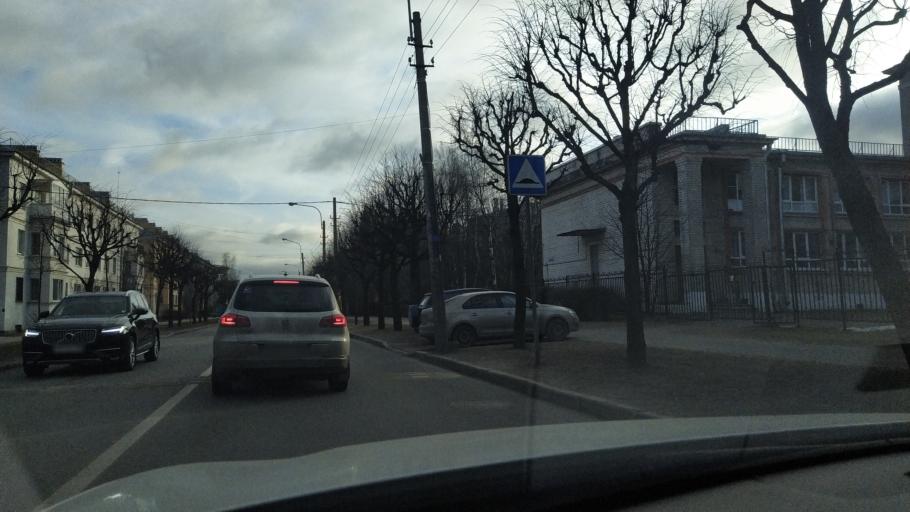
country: RU
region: St.-Petersburg
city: Pushkin
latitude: 59.7245
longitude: 30.4239
